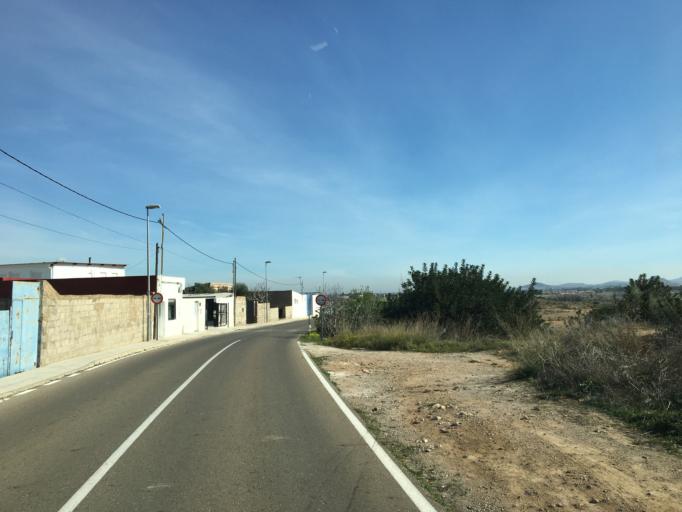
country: ES
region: Murcia
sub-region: Murcia
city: Cartagena
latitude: 37.6294
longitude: -1.0345
